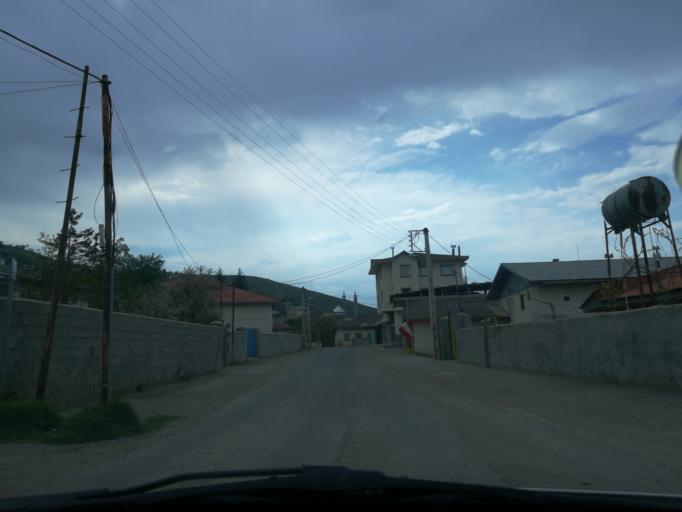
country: IR
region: Mazandaran
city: `Abbasabad
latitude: 36.5320
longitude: 51.2262
